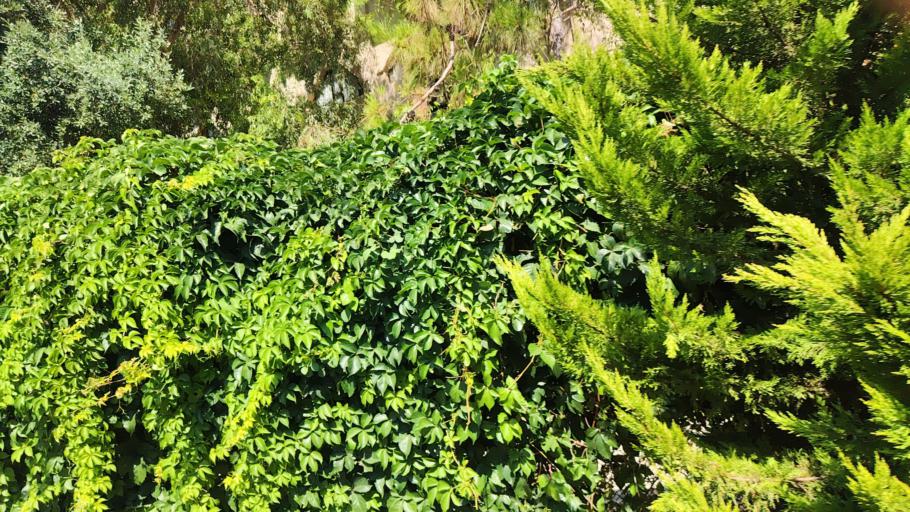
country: TR
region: Mugla
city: Sarigerme
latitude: 36.7033
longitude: 28.6954
